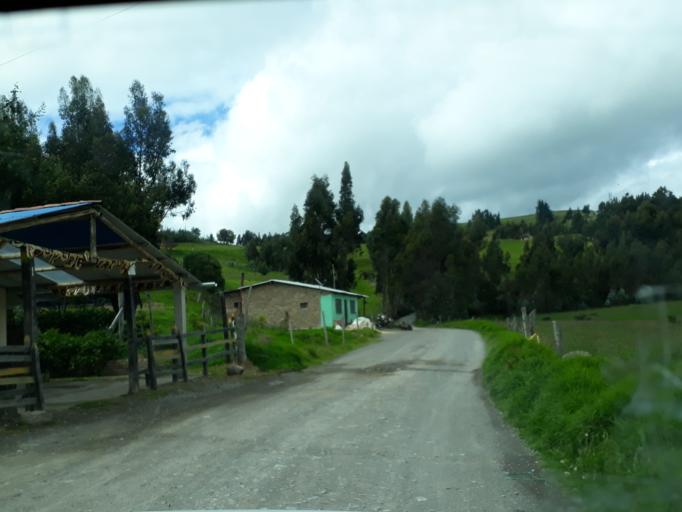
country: CO
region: Cundinamarca
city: La Mesa
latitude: 5.3057
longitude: -73.9021
